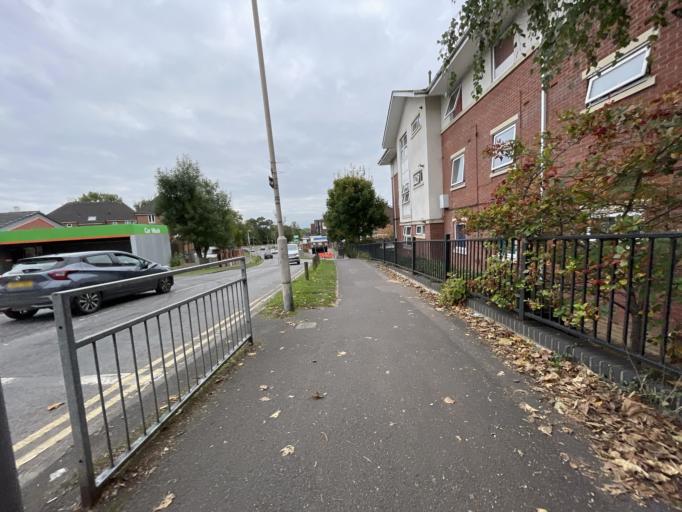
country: GB
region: England
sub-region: West Berkshire
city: Tilehurst
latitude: 51.4507
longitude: -1.0167
